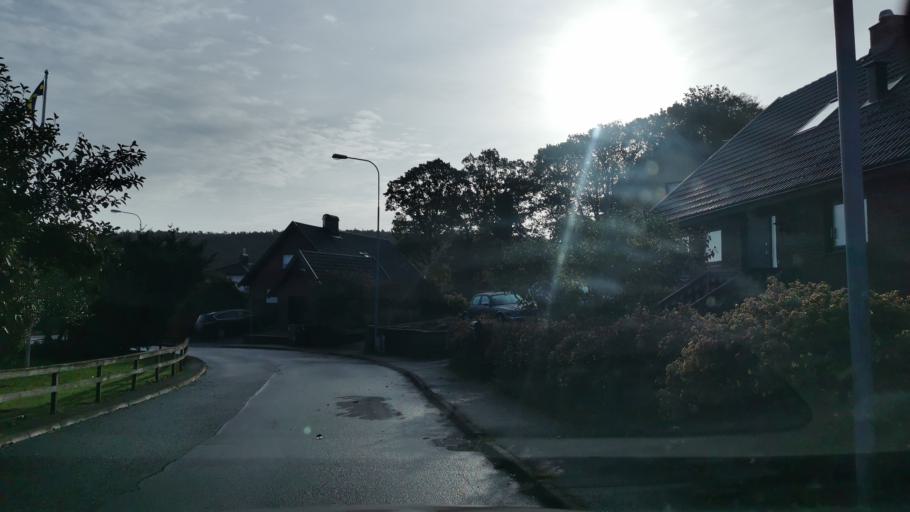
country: SE
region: Vaestra Goetaland
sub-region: Partille Kommun
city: Partille
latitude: 57.7276
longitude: 12.0870
